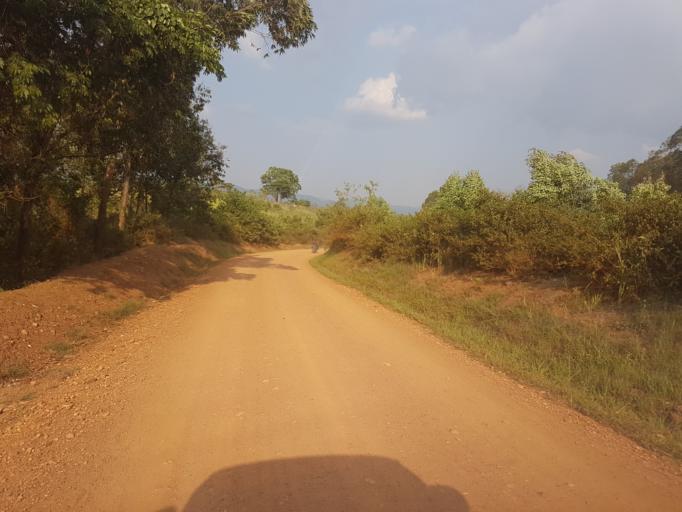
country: UG
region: Western Region
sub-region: Rukungiri District
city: Rukungiri
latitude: -0.6521
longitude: 29.8591
